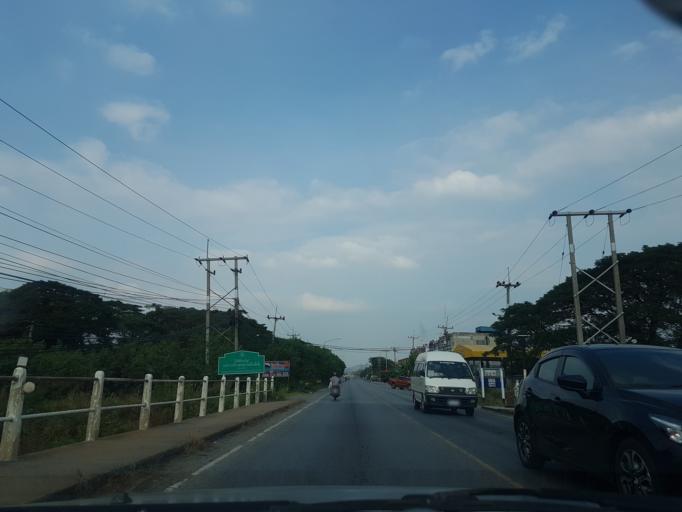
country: TH
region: Sara Buri
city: Ban Mo
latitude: 14.6082
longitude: 100.7387
